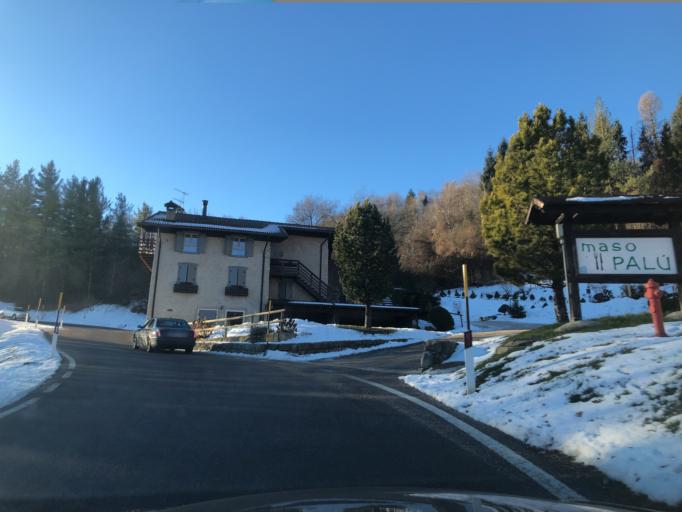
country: IT
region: Trentino-Alto Adige
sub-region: Provincia di Trento
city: Brentonico
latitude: 45.8122
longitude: 10.9410
